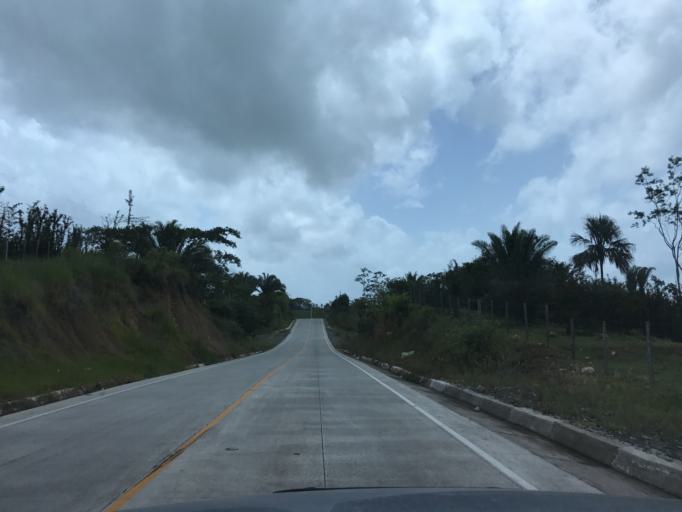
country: GT
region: Izabal
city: Morales
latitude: 15.6249
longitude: -89.0598
